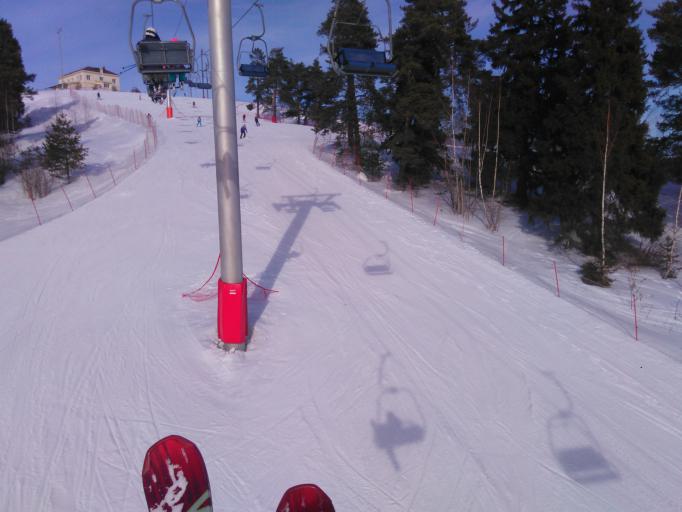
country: RU
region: Moskovskaya
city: Dedenevo
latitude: 56.2708
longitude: 37.5614
